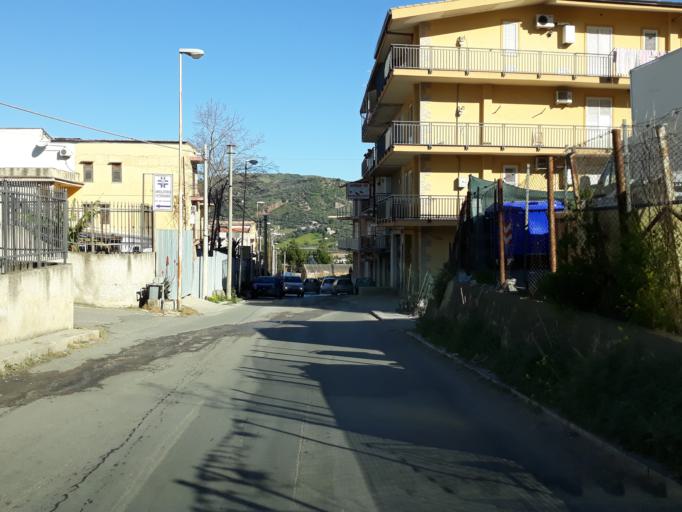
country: IT
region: Sicily
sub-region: Palermo
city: Misilmeri
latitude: 38.0279
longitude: 13.4519
